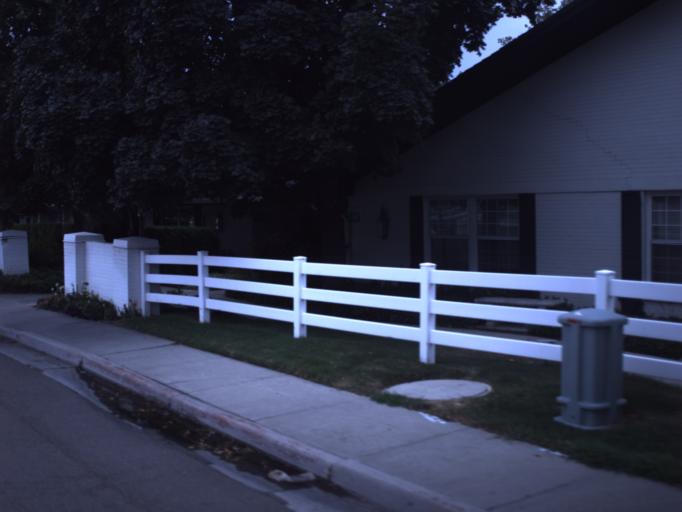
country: US
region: Utah
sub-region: Salt Lake County
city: Millcreek
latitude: 40.6854
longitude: -111.8716
